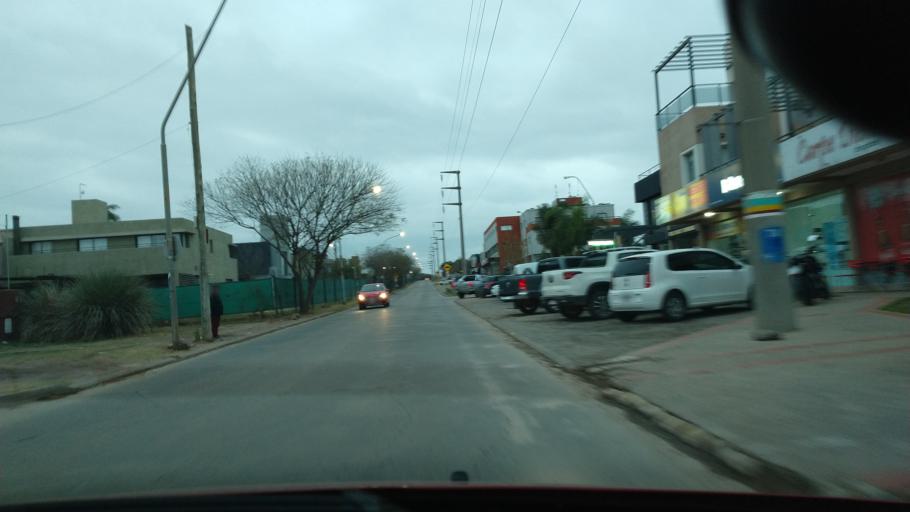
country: AR
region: Cordoba
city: La Calera
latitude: -31.3785
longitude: -64.2710
